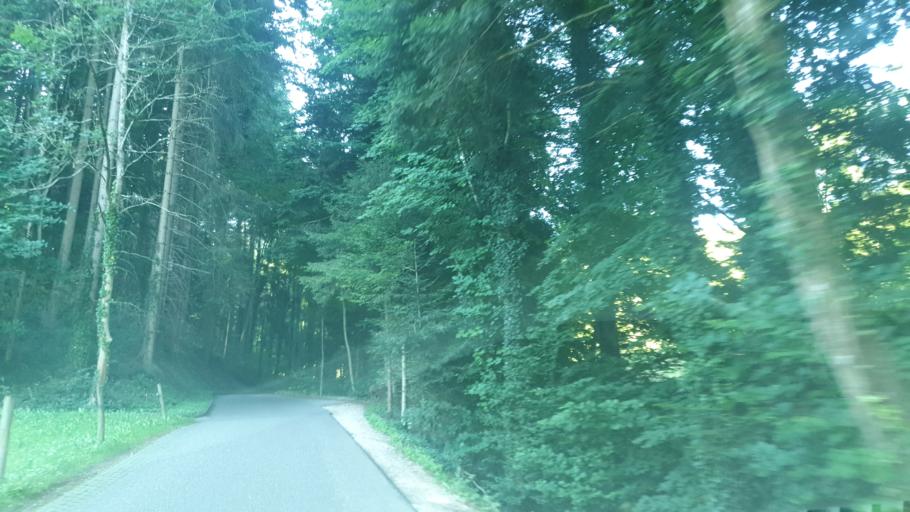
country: DE
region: Baden-Wuerttemberg
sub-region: Freiburg Region
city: Au
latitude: 47.9402
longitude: 7.8438
